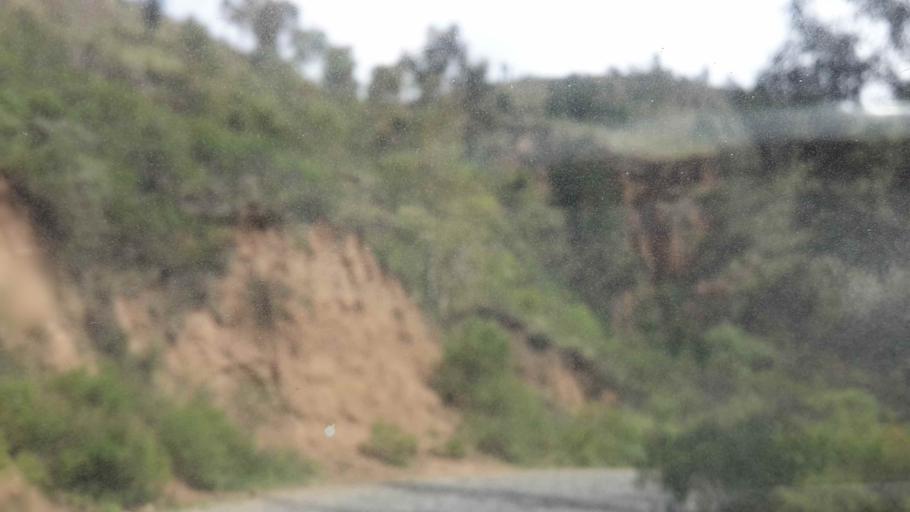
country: BO
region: Cochabamba
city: Cochabamba
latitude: -17.3633
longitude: -66.0643
